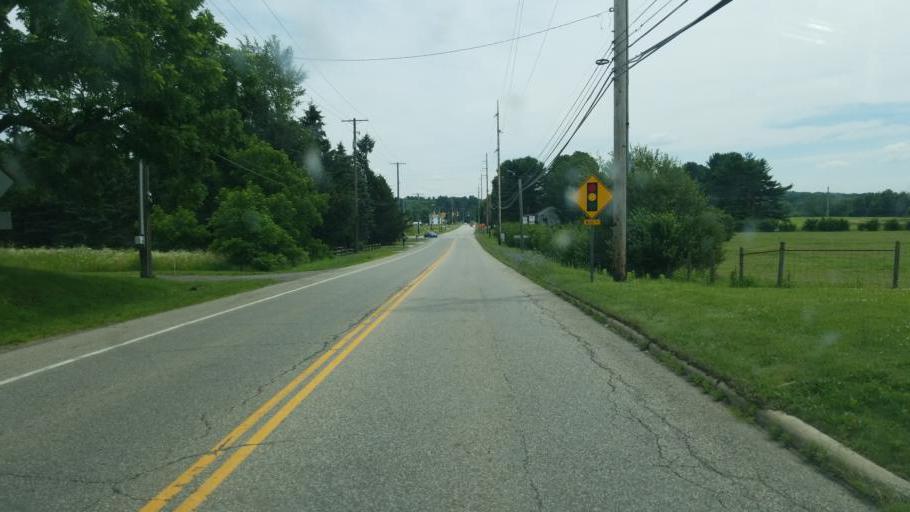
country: US
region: Ohio
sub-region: Geauga County
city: Bainbridge
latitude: 41.3882
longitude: -81.2768
